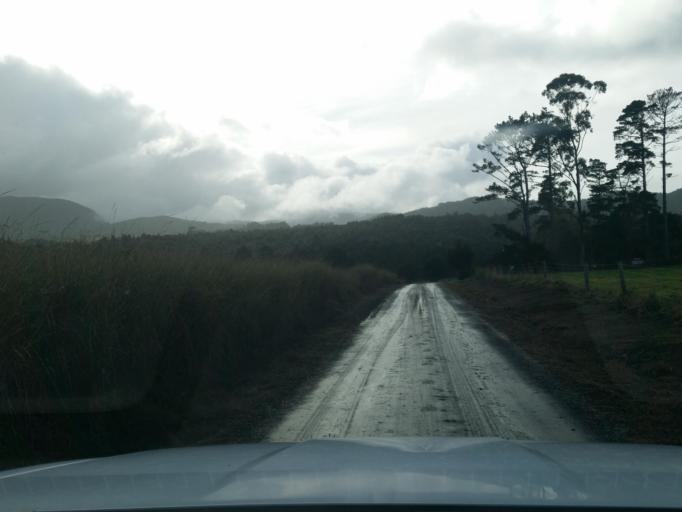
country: NZ
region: Northland
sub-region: Kaipara District
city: Dargaville
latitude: -35.8027
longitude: 173.7416
